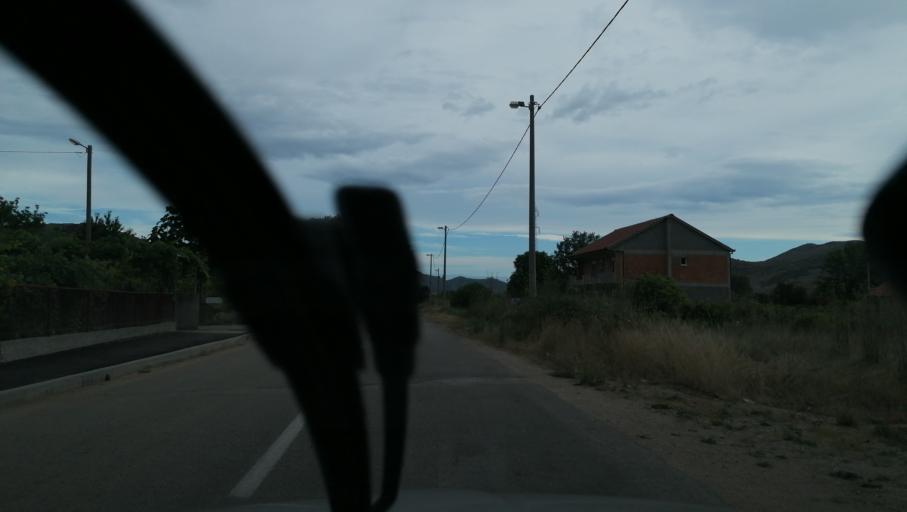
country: BA
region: Republika Srpska
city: Trebinje
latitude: 42.6817
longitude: 18.3340
